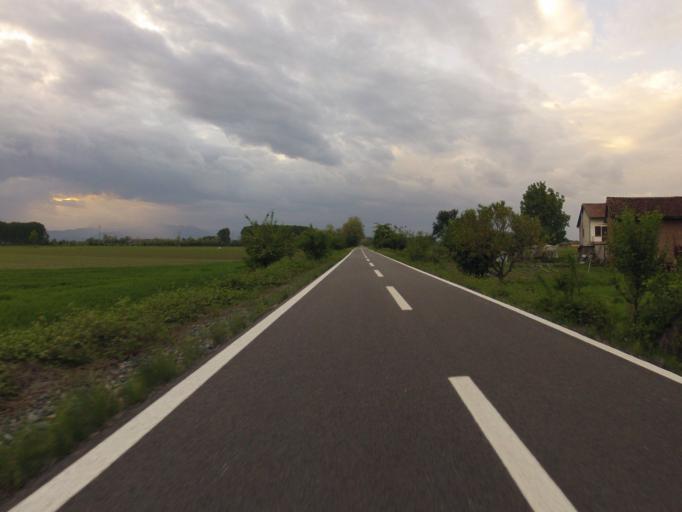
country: IT
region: Piedmont
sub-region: Provincia di Torino
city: Vigone
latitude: 44.8171
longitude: 7.4977
